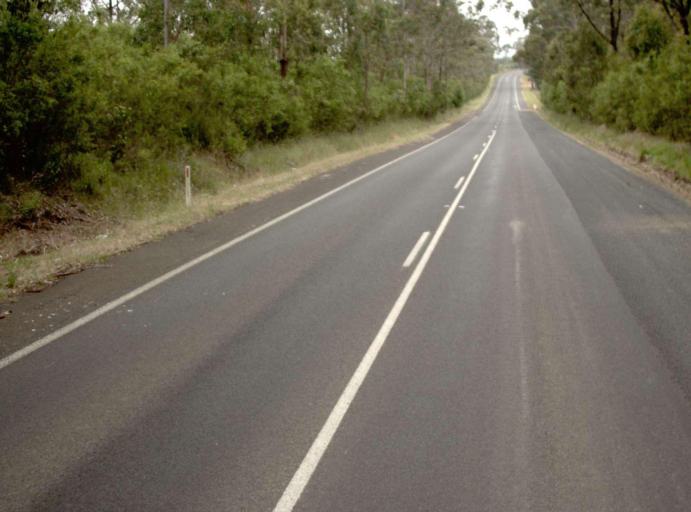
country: AU
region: Victoria
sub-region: Latrobe
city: Moe
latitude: -38.3100
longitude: 146.2700
